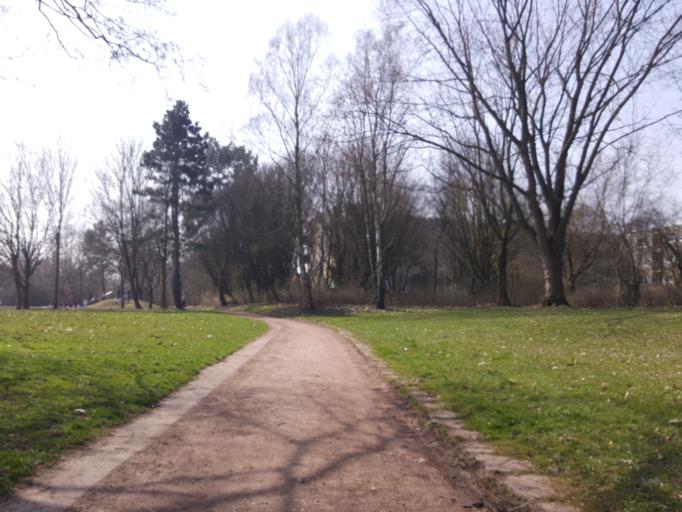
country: DE
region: Schleswig-Holstein
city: Oststeinbek
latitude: 53.5310
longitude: 10.1564
